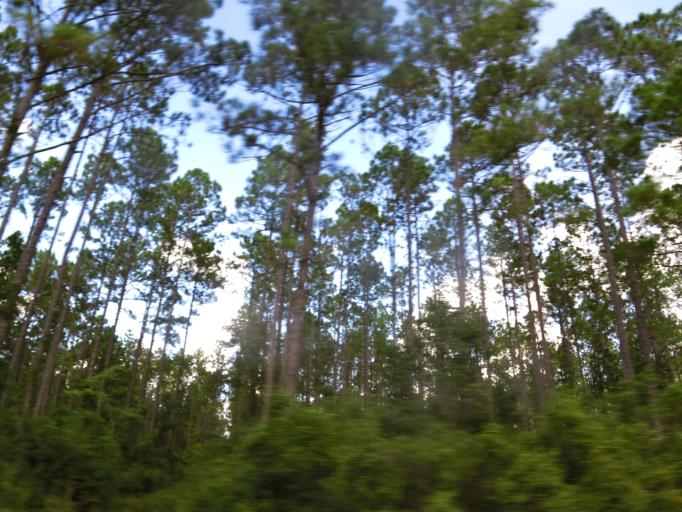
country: US
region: Georgia
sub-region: Echols County
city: Statenville
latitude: 30.7535
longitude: -83.1138
